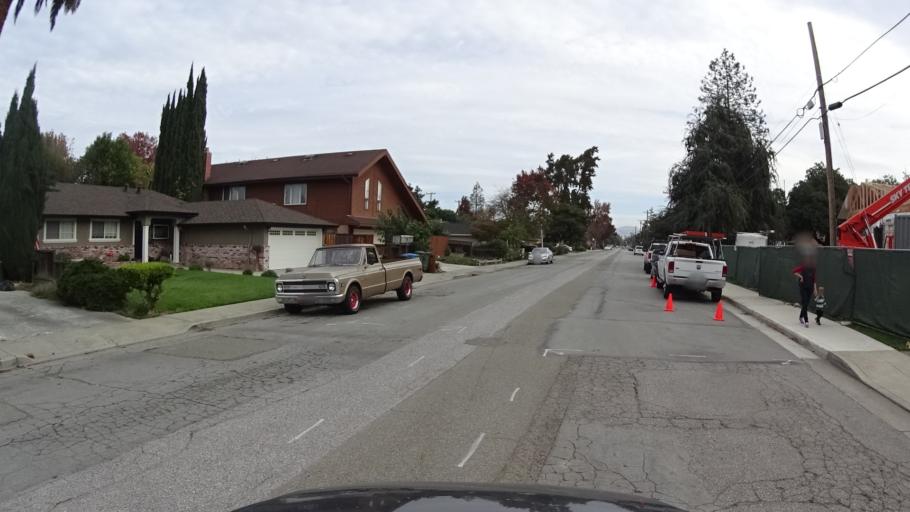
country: US
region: California
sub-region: Santa Clara County
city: Santa Clara
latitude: 37.3270
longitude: -121.9640
